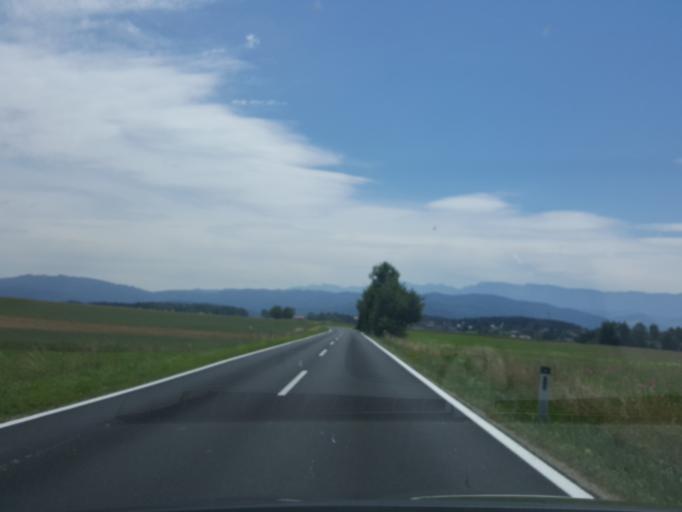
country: AT
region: Upper Austria
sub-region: Politischer Bezirk Vocklabruck
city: Gampern
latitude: 47.9724
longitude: 13.5640
